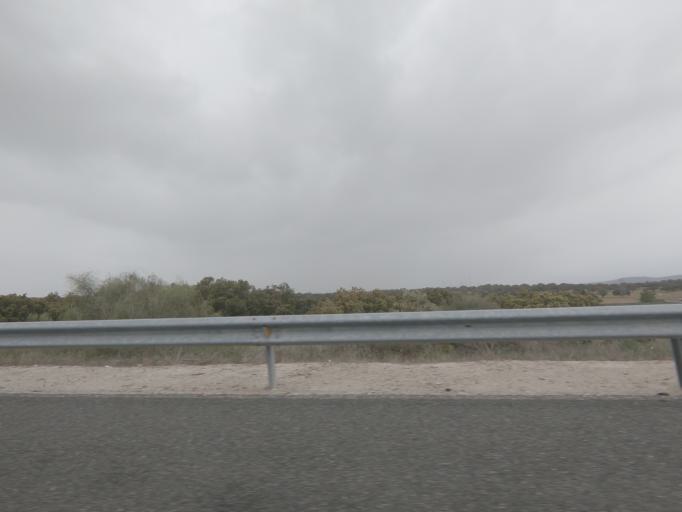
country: ES
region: Extremadura
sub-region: Provincia de Caceres
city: Villar de Plasencia
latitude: 40.1480
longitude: -6.0385
